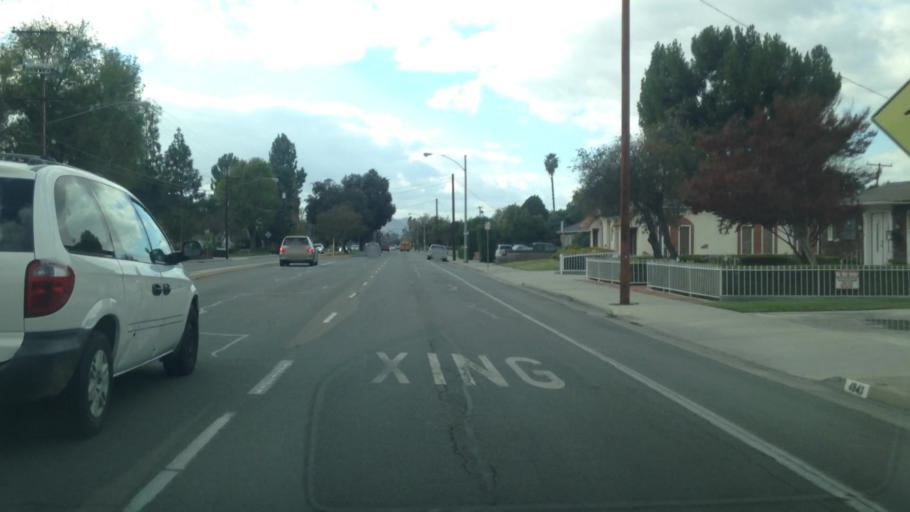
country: US
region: California
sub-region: Riverside County
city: Riverside
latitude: 33.9462
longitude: -117.4086
